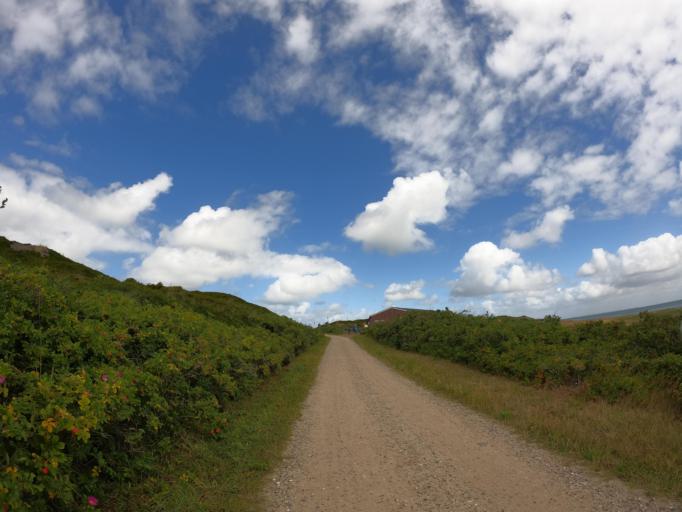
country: DE
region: Schleswig-Holstein
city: Tinnum
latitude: 54.7982
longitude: 8.2925
